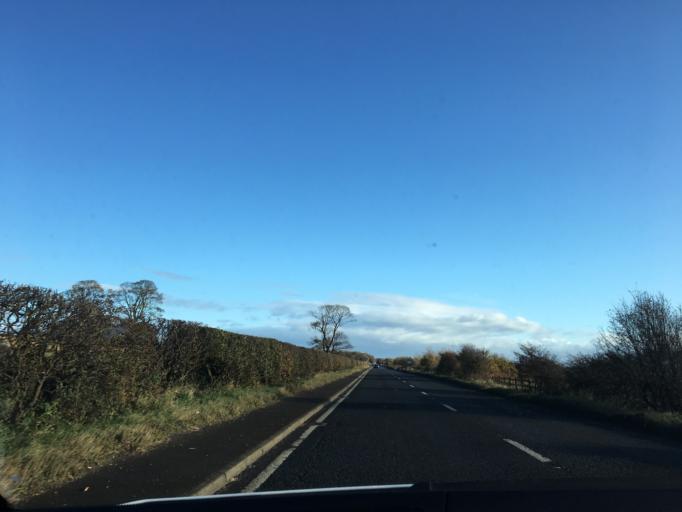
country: GB
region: Scotland
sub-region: East Lothian
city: Haddington
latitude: 55.9690
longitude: -2.7430
